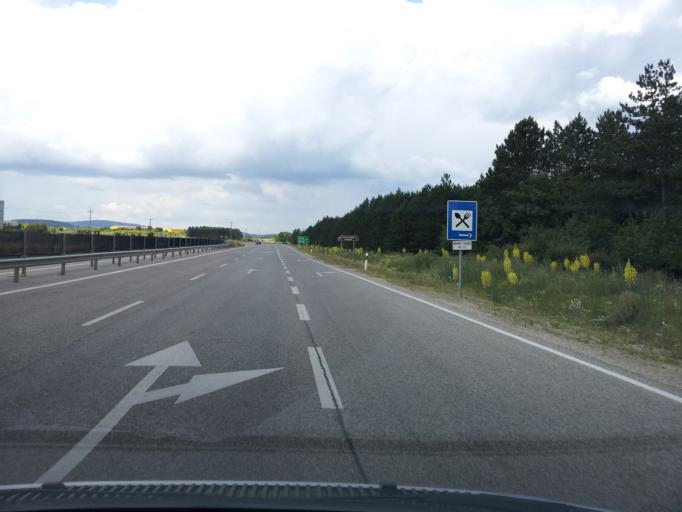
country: HU
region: Veszprem
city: Nemesvamos
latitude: 47.1199
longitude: 17.8355
